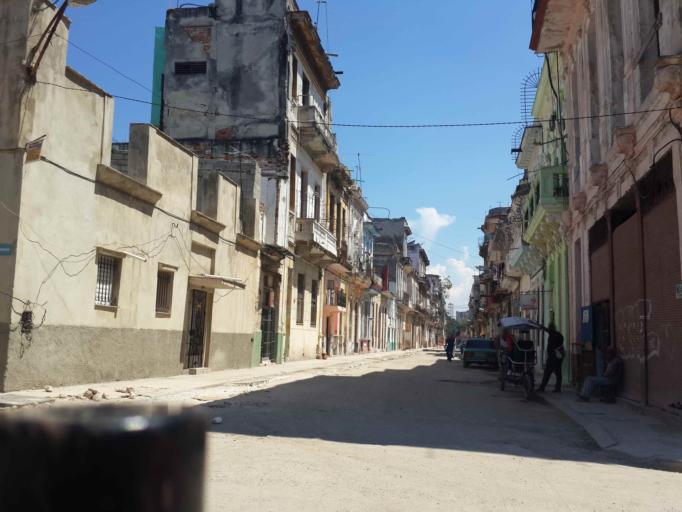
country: CU
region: La Habana
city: Centro Habana
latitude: 23.1400
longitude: -82.3624
